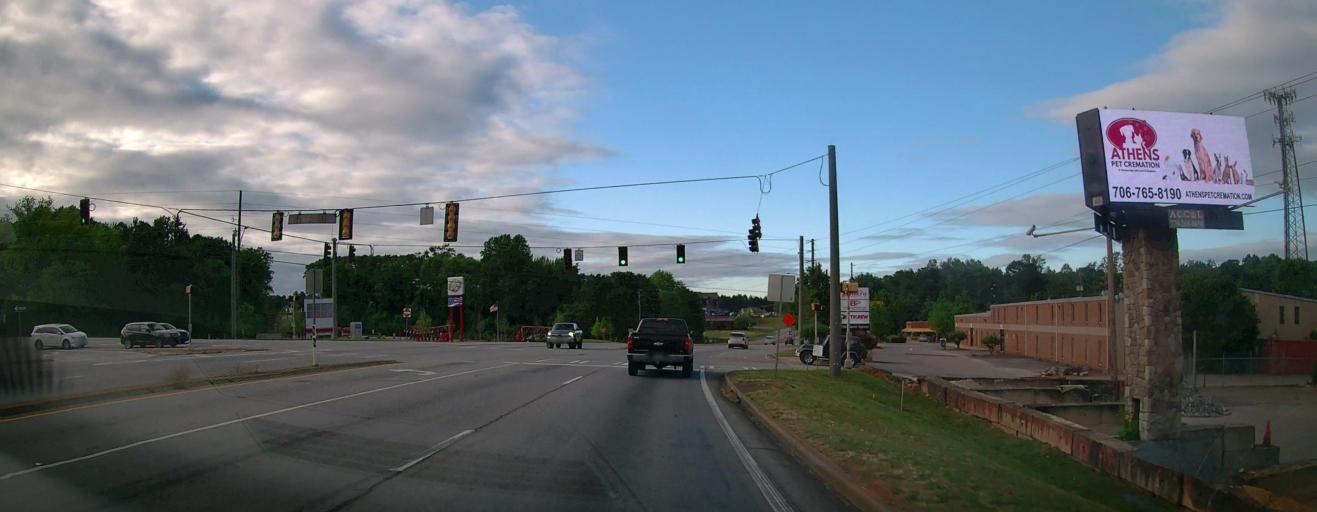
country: US
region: Georgia
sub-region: Oconee County
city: Watkinsville
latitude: 33.8884
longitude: -83.4139
